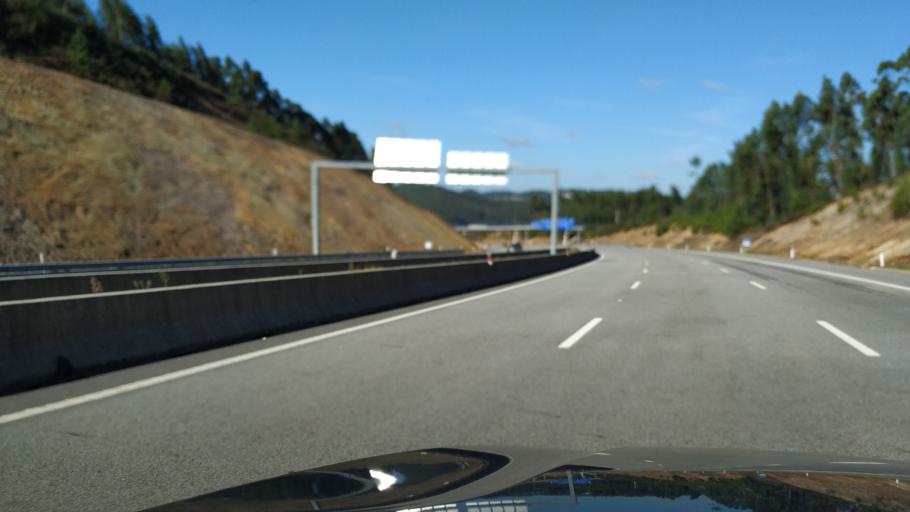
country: PT
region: Porto
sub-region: Vila Nova de Gaia
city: Sandim
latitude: 41.0275
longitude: -8.4804
